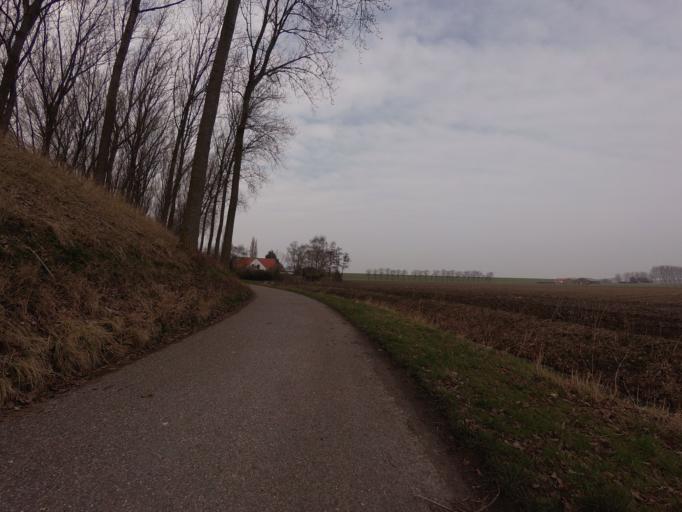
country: BE
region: Flanders
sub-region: Provincie Oost-Vlaanderen
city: Sint-Gillis-Waas
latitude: 51.3305
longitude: 4.1885
